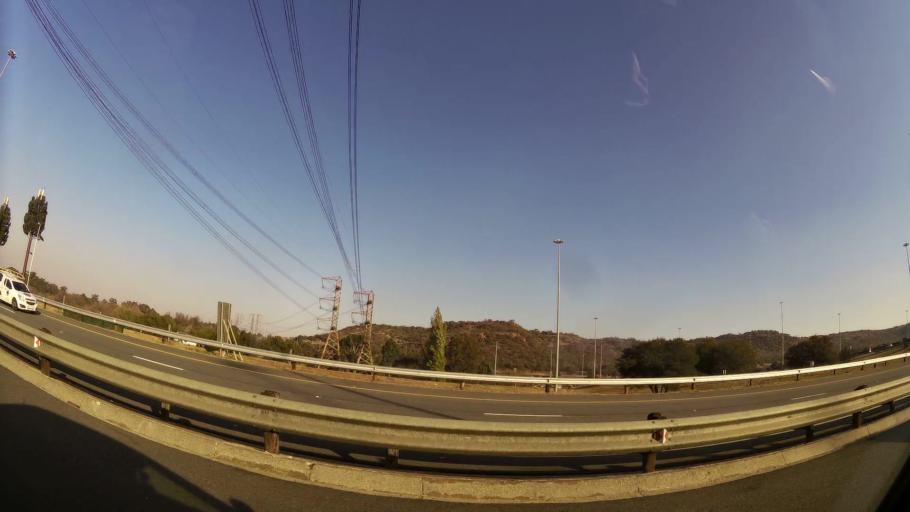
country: ZA
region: Gauteng
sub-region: City of Johannesburg Metropolitan Municipality
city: Johannesburg
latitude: -26.2639
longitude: 28.0973
